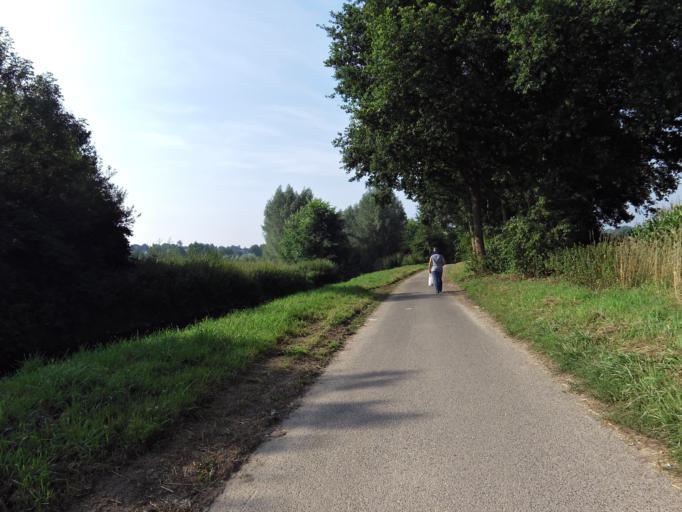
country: DE
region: North Rhine-Westphalia
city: Geilenkirchen
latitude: 50.9533
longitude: 6.1089
